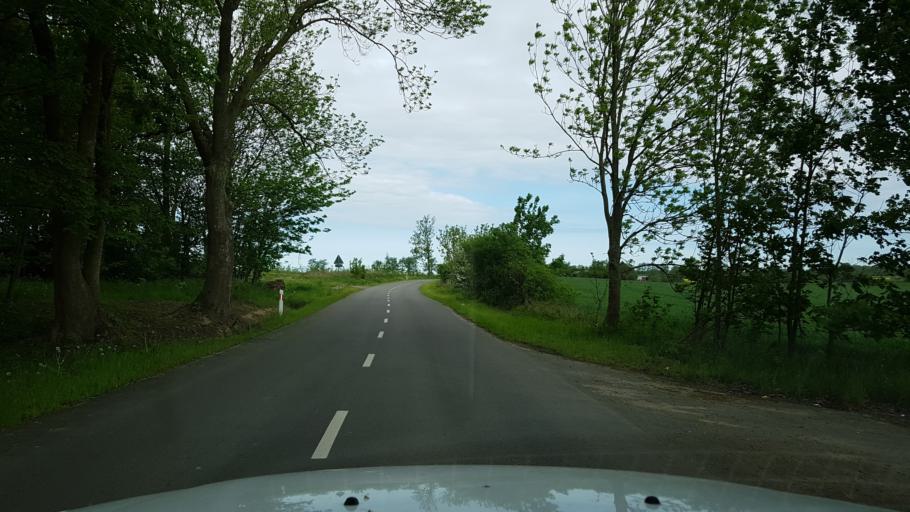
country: PL
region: West Pomeranian Voivodeship
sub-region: Powiat kolobrzeski
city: Ustronie Morskie
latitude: 54.2074
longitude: 15.8298
